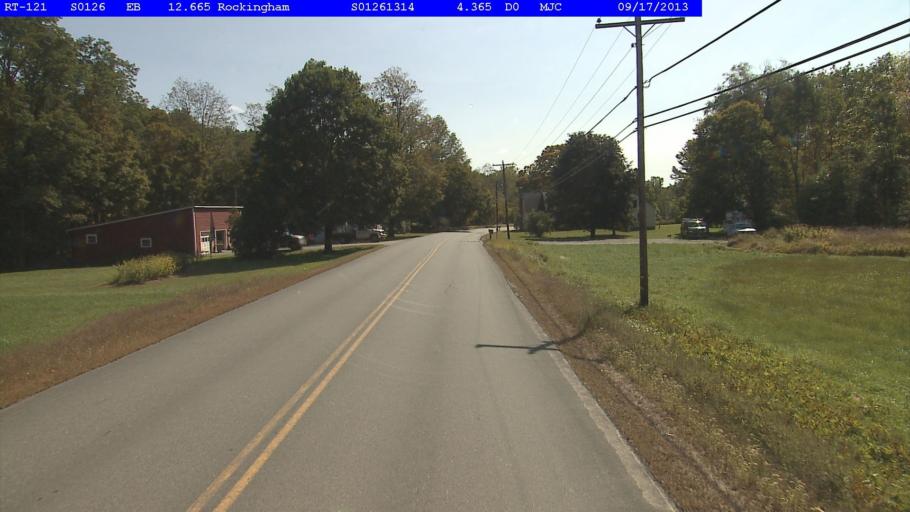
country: US
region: Vermont
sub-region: Windham County
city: Bellows Falls
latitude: 43.1360
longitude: -72.4853
